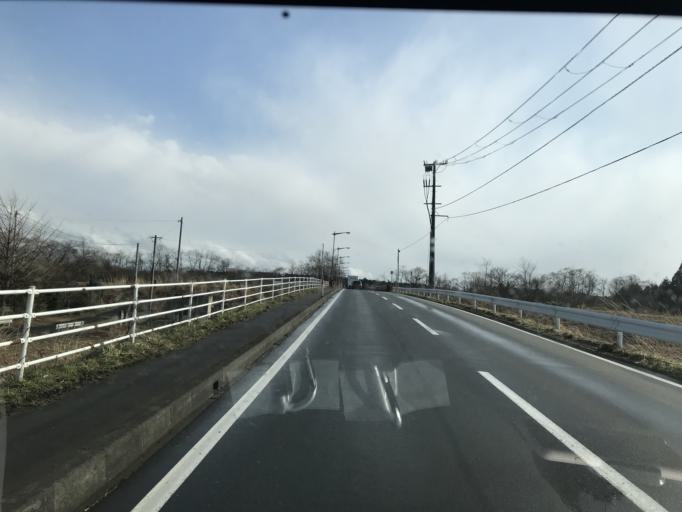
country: JP
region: Iwate
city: Kitakami
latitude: 39.2922
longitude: 141.0550
